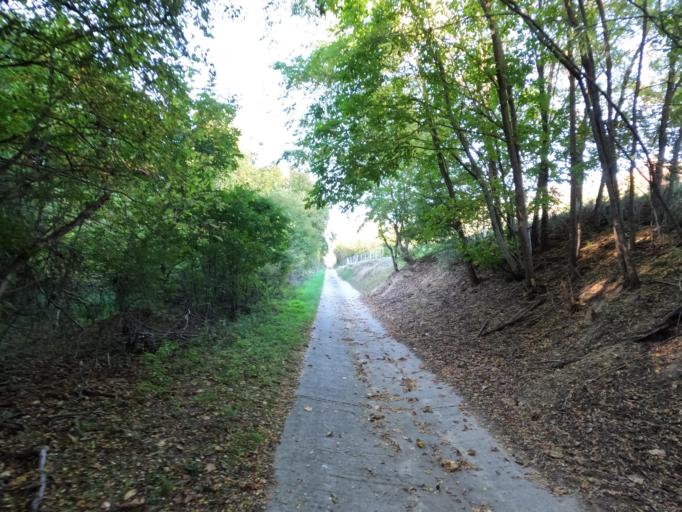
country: HU
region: Tolna
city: Szekszard
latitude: 46.3037
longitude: 18.6619
